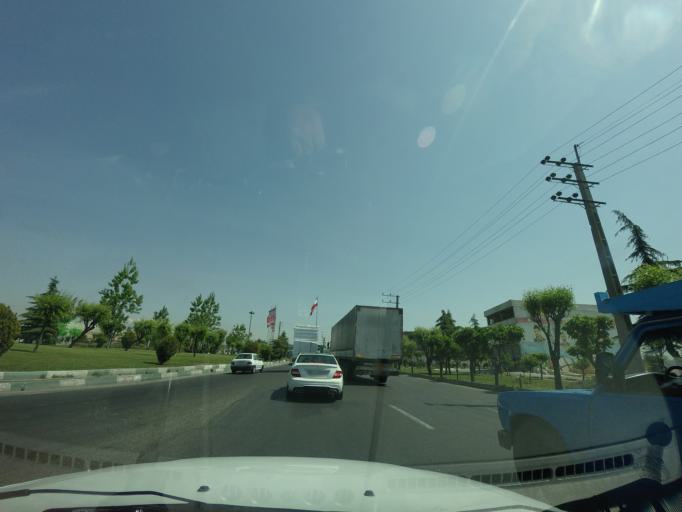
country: IR
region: Tehran
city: Eslamshahr
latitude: 35.6160
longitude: 51.3160
